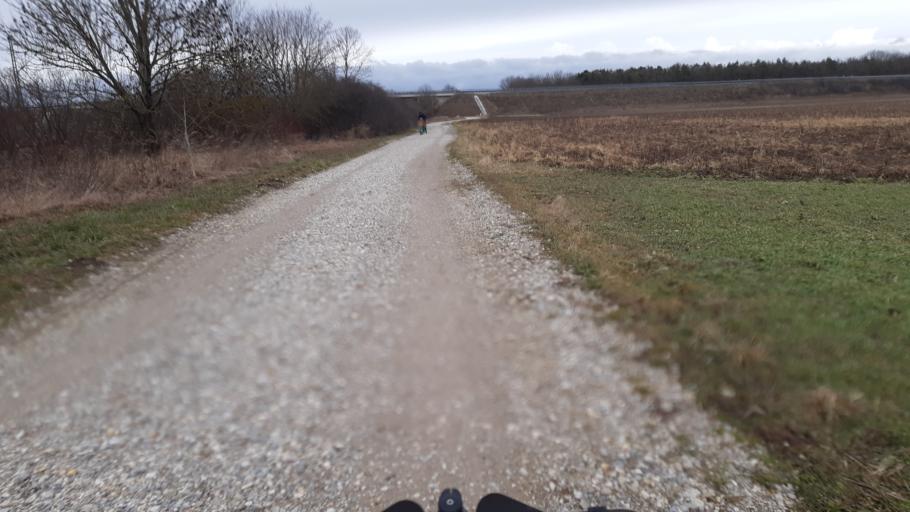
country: DE
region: Bavaria
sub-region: Upper Bavaria
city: Oberschleissheim
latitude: 48.2239
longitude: 11.5423
